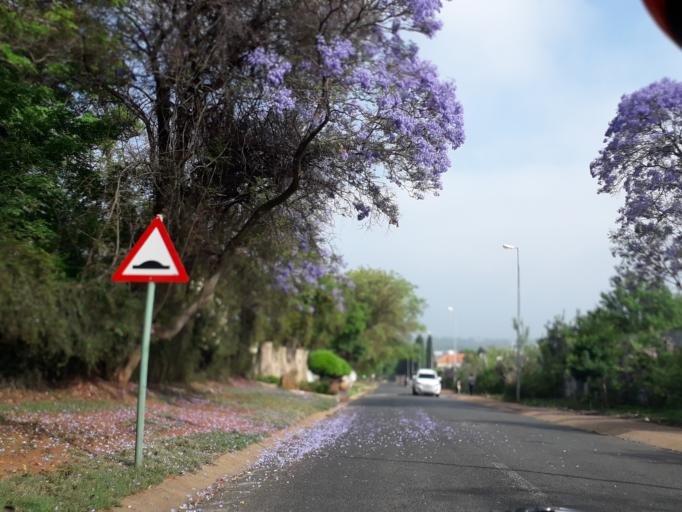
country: ZA
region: Gauteng
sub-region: City of Johannesburg Metropolitan Municipality
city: Johannesburg
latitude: -26.0858
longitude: 28.0346
